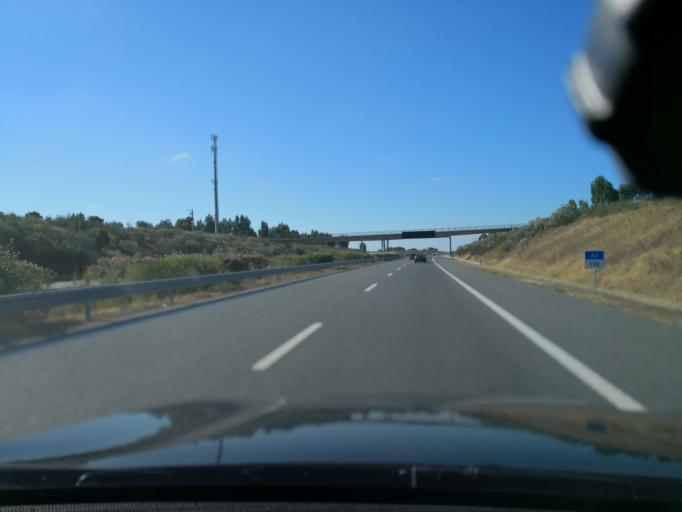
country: PT
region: Beja
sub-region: Ourique
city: Ourique
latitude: 37.6846
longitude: -8.1649
